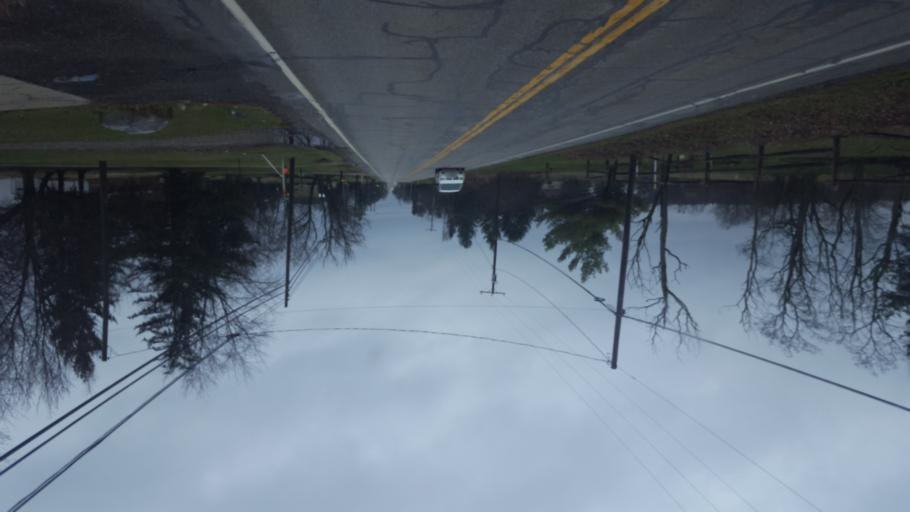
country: US
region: Ohio
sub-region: Medina County
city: Medina
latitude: 41.0843
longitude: -81.8642
